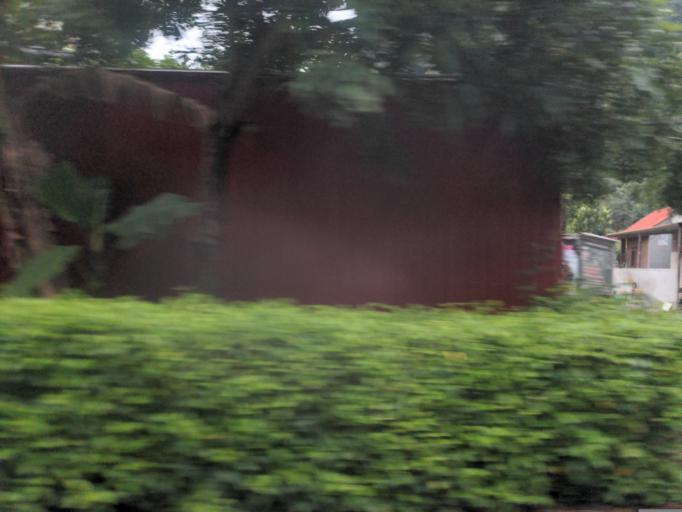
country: VN
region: Ninh Binh
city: Thi Tran Tam Diep
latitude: 20.2158
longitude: 105.9170
